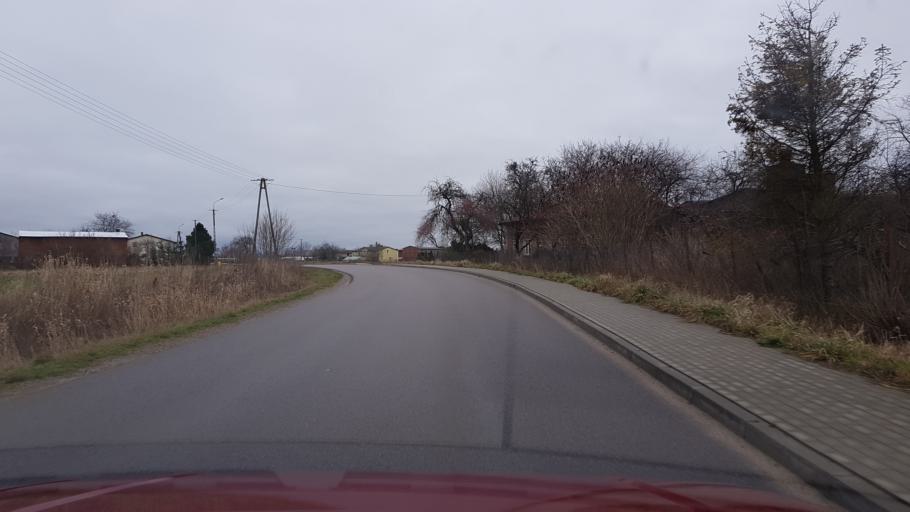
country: PL
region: West Pomeranian Voivodeship
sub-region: Powiat koszalinski
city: Mielno
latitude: 54.1679
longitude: 16.0275
